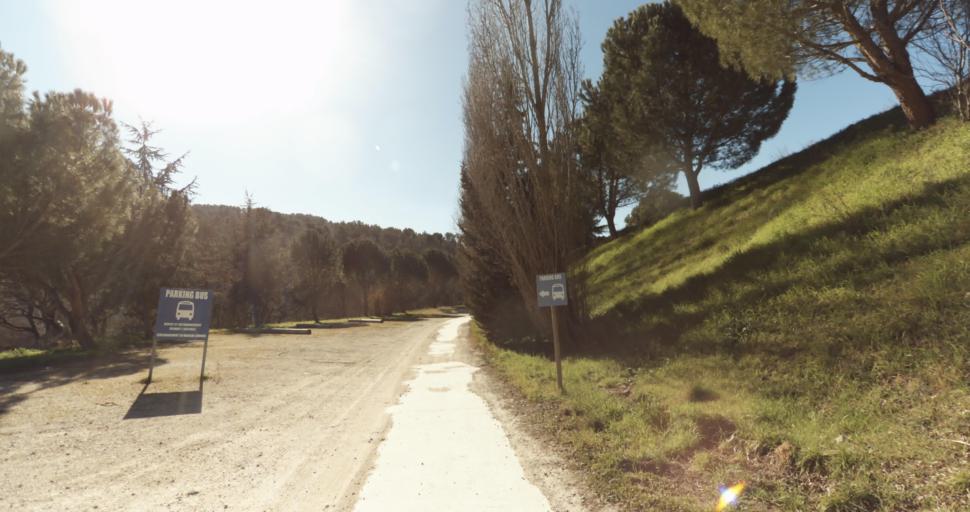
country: FR
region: Provence-Alpes-Cote d'Azur
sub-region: Departement des Bouches-du-Rhone
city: Peypin
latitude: 43.3948
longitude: 5.5644
